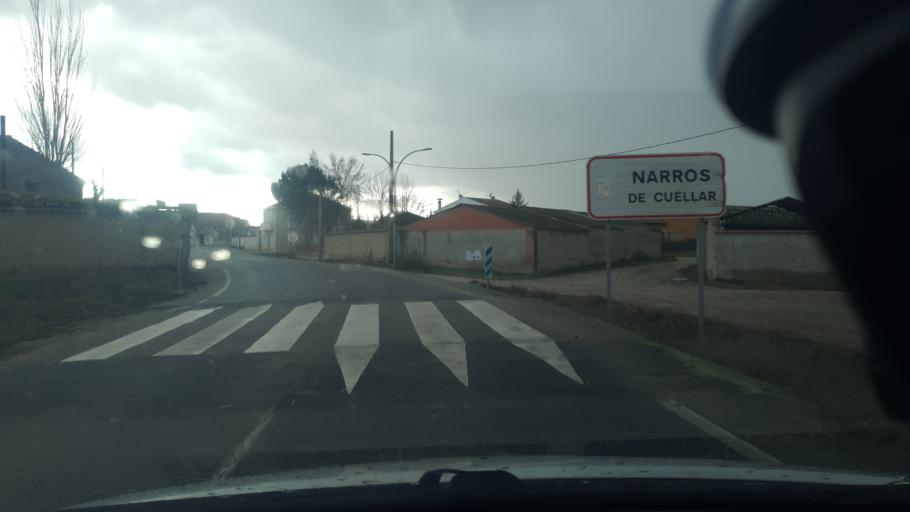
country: ES
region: Castille and Leon
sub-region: Provincia de Segovia
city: Chane
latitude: 41.3012
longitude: -4.4057
